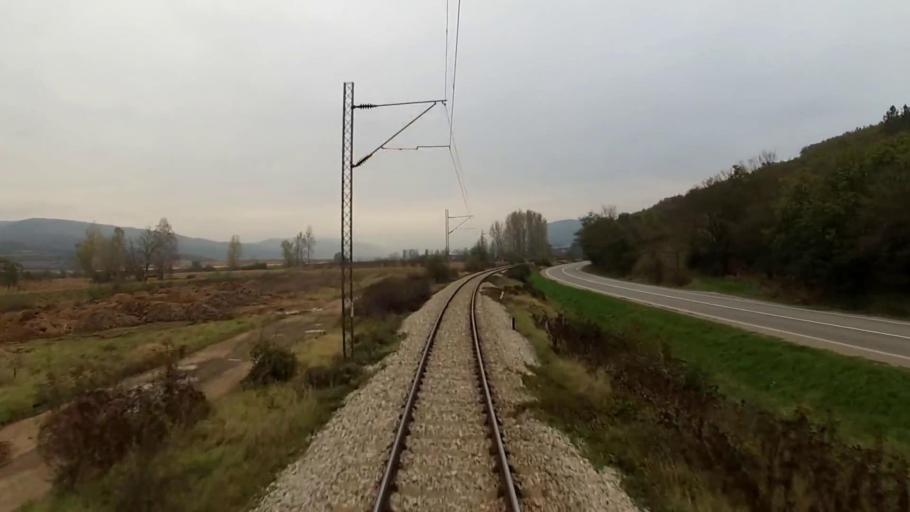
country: RS
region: Central Serbia
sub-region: Pirotski Okrug
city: Dimitrovgrad
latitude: 43.0111
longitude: 22.8002
